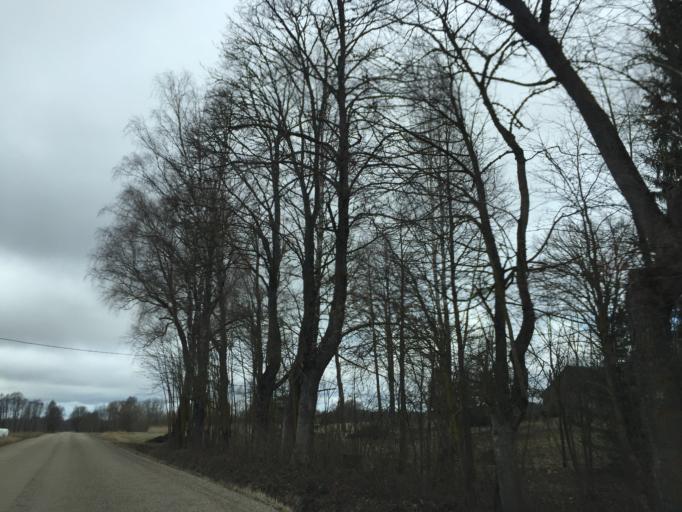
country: LV
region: Ilukste
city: Ilukste
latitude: 56.0603
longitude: 26.1641
